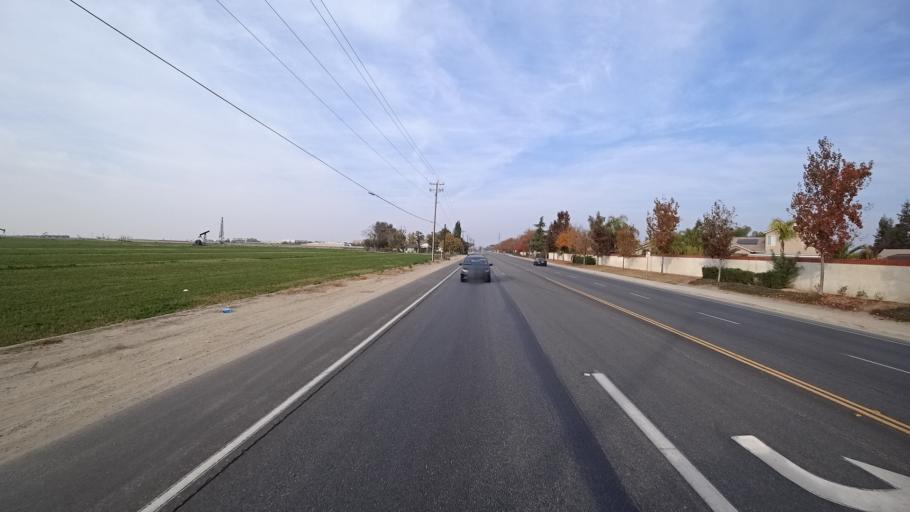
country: US
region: California
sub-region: Kern County
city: Greenacres
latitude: 35.3067
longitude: -119.1281
